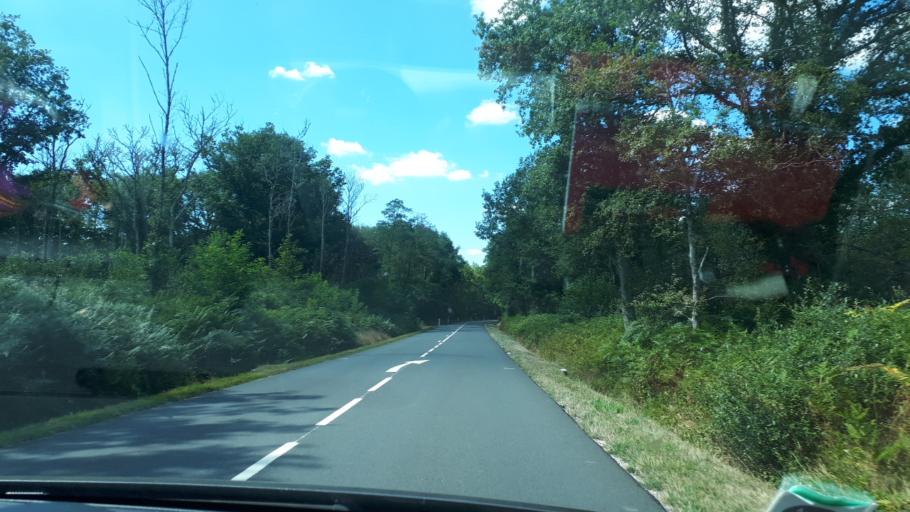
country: FR
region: Centre
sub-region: Departement du Loir-et-Cher
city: Saint-Viatre
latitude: 47.5635
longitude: 1.9072
